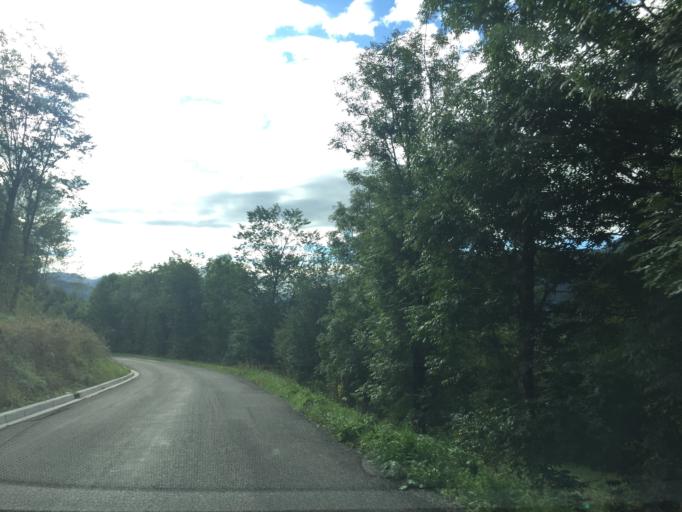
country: FR
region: Midi-Pyrenees
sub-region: Departement de la Haute-Garonne
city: Bagneres-de-Luchon
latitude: 42.8110
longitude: 0.4952
